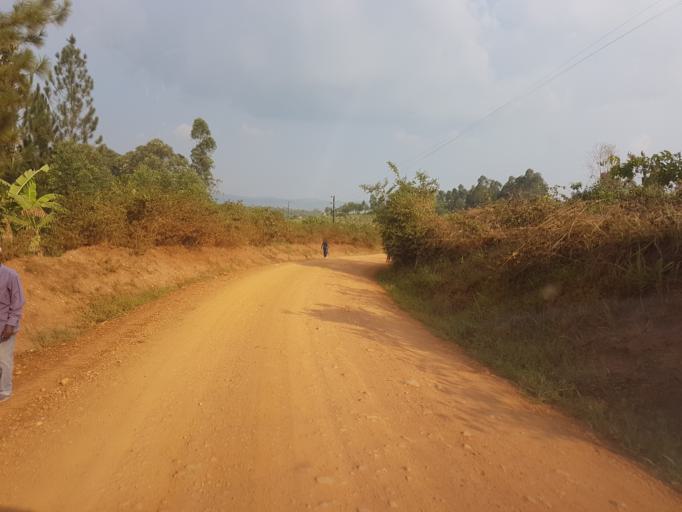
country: UG
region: Western Region
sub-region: Rukungiri District
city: Rukungiri
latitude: -0.6582
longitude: 29.8625
